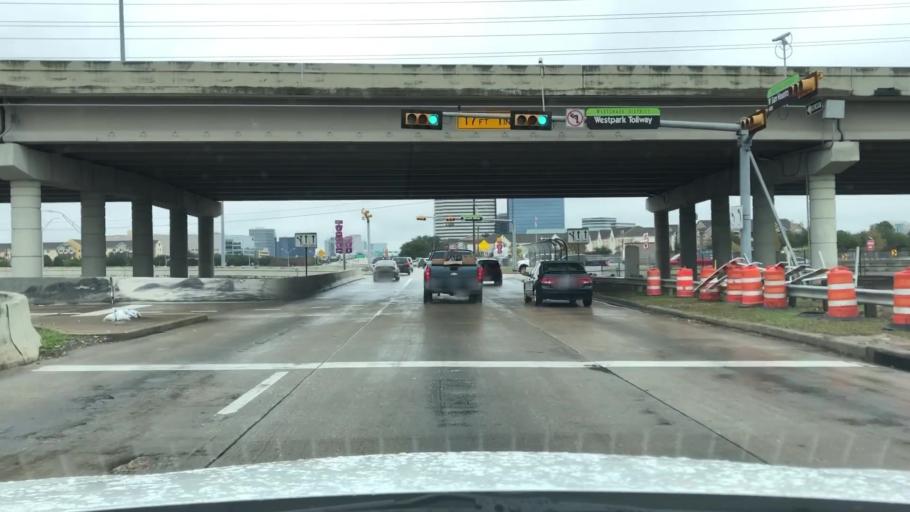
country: US
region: Texas
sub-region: Harris County
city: Bunker Hill Village
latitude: 29.7179
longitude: -95.5565
